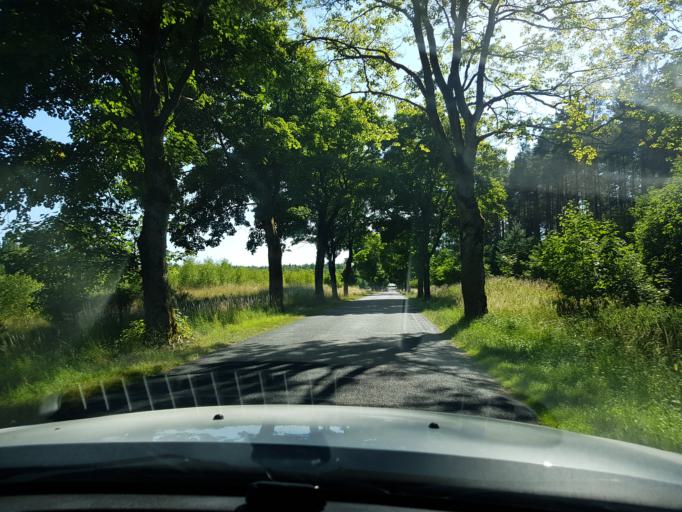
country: PL
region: West Pomeranian Voivodeship
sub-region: Powiat swidwinski
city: Slawoborze
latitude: 53.9146
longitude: 15.7807
